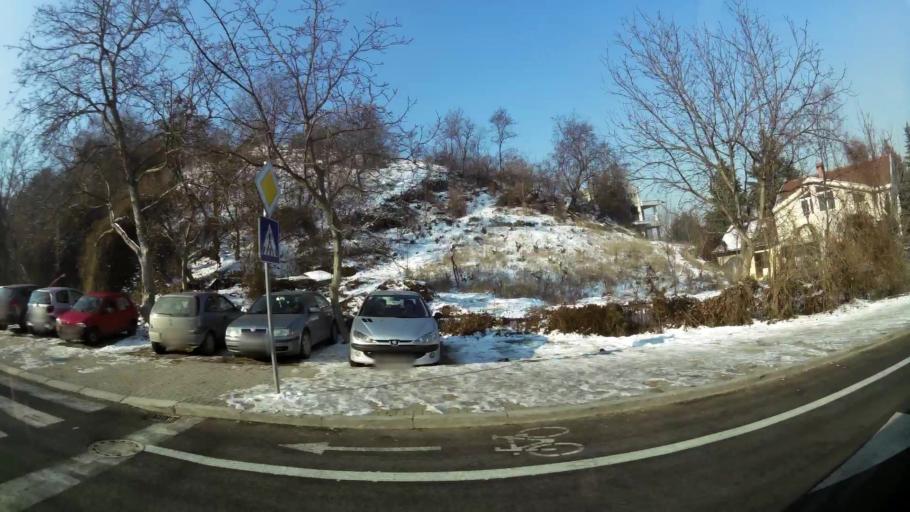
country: MK
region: Karpos
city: Skopje
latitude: 41.9842
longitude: 21.4188
